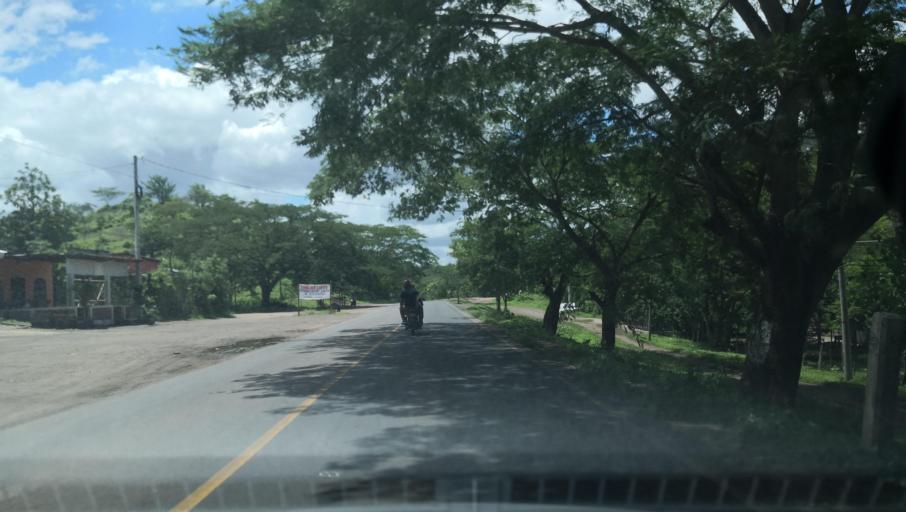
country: NI
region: Esteli
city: Condega
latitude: 13.3791
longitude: -86.4017
